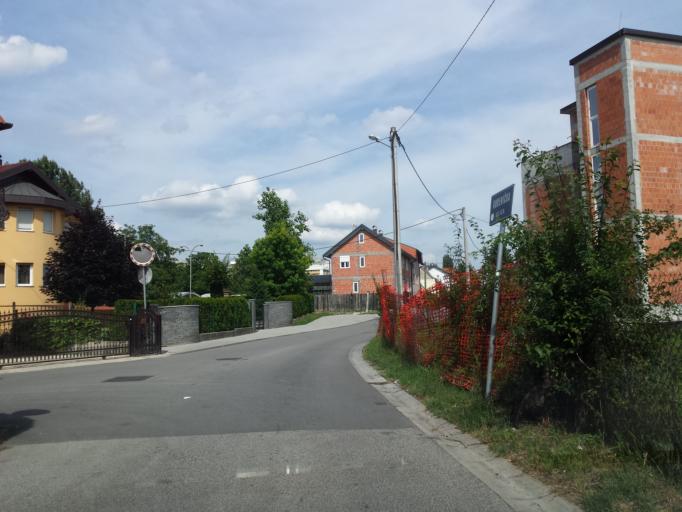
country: HR
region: Grad Zagreb
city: Jankomir
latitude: 45.7994
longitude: 15.9240
